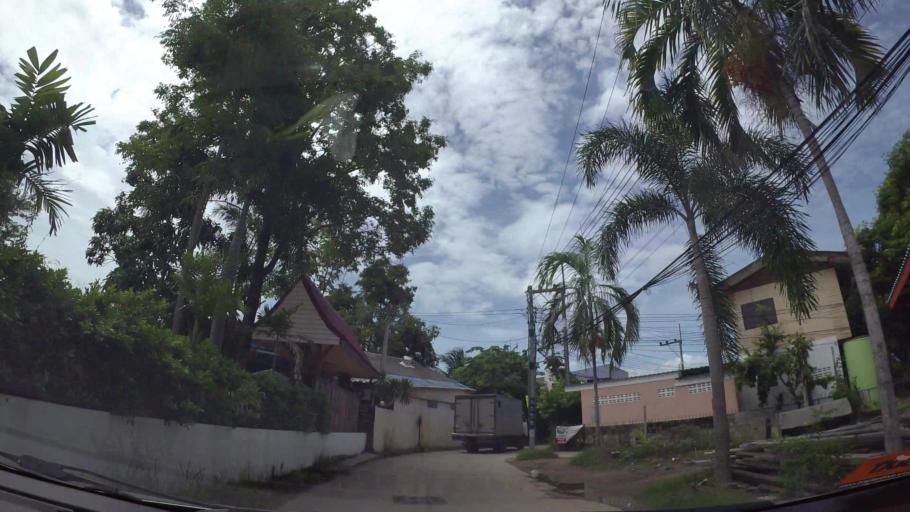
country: TH
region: Chon Buri
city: Sattahip
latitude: 12.7036
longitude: 100.8880
